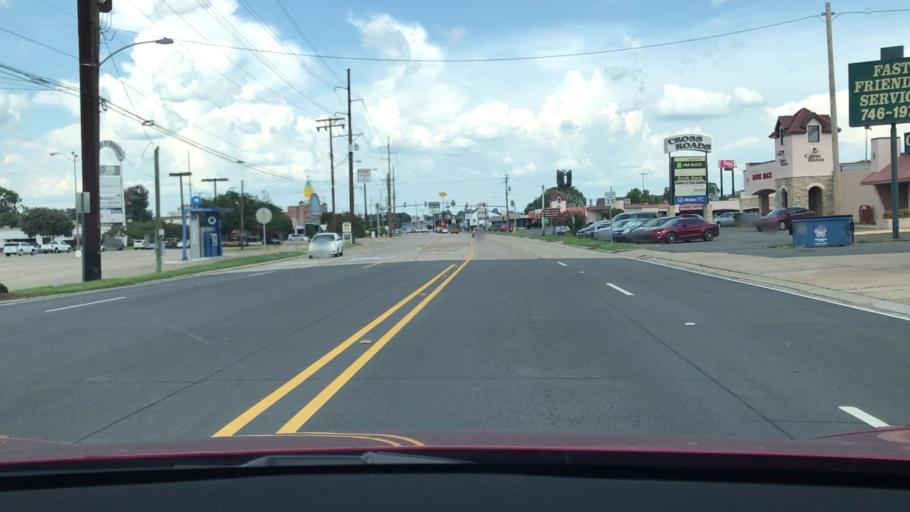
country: US
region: Louisiana
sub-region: Bossier Parish
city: Bossier City
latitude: 32.5158
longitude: -93.7188
